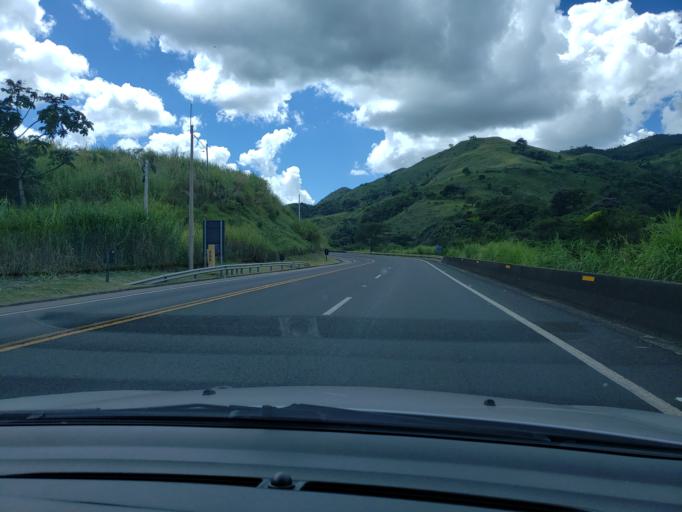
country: BR
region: Sao Paulo
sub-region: Sao Joao Da Boa Vista
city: Sao Joao da Boa Vista
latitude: -21.8984
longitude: -46.6965
